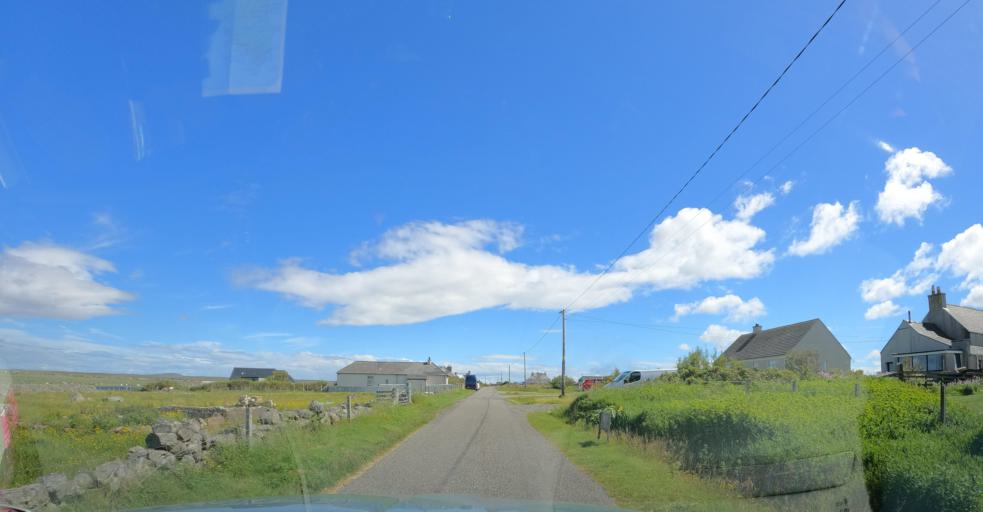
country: GB
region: Scotland
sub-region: Eilean Siar
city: Isle of Lewis
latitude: 58.3583
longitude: -6.5590
